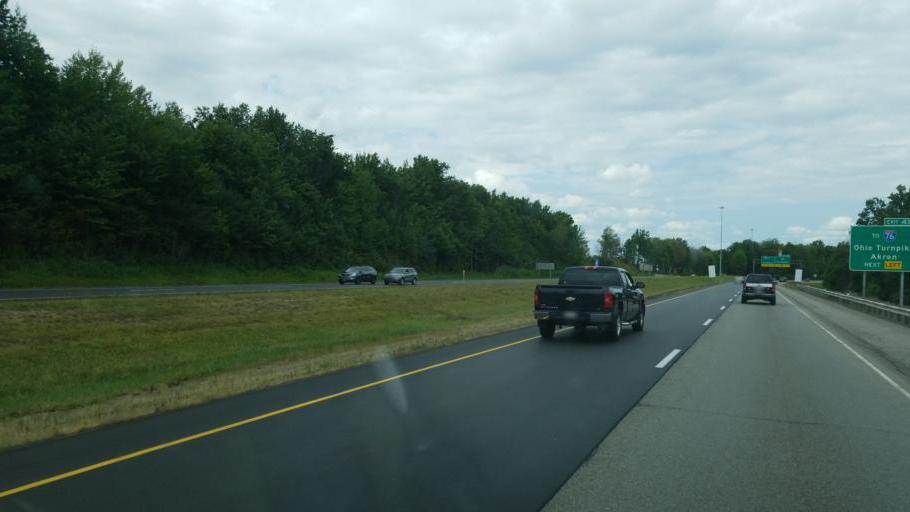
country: US
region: Ohio
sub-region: Mahoning County
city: Austintown
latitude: 41.1141
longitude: -80.7548
